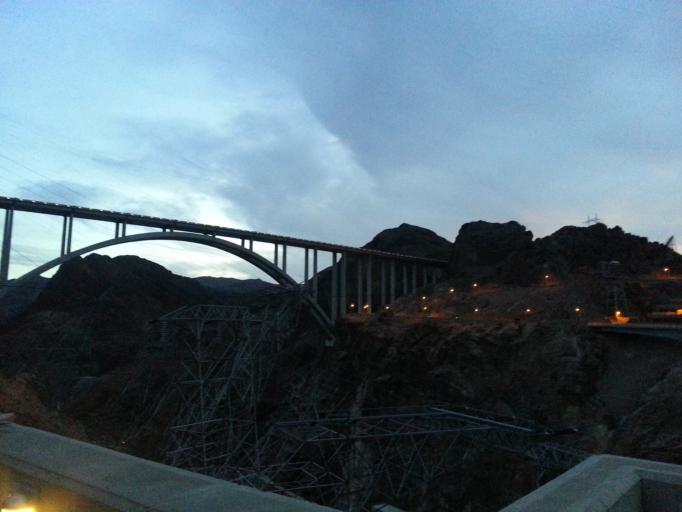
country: US
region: Nevada
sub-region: Clark County
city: Boulder City
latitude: 36.0149
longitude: -114.7371
